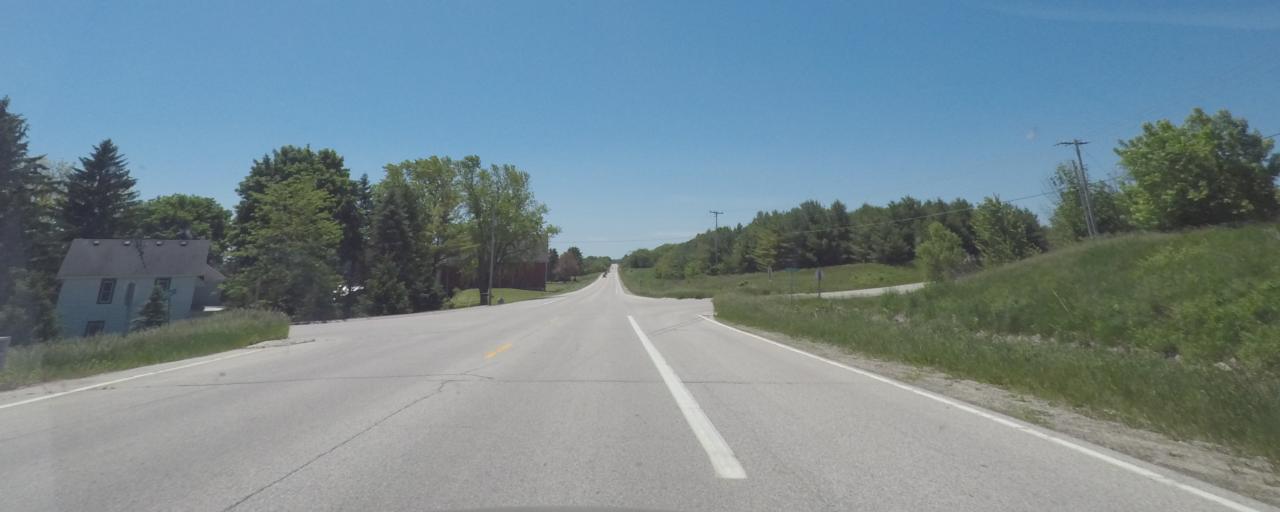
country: US
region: Wisconsin
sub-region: Ozaukee County
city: Kohler
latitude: 43.5719
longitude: -88.0623
